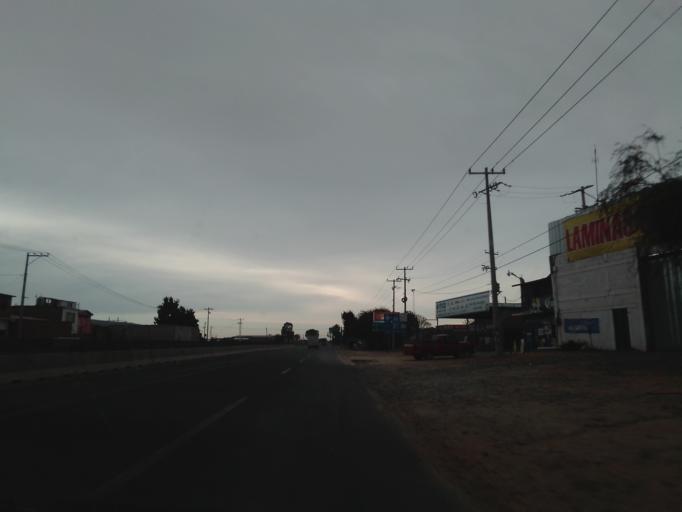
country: MX
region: Guanajuato
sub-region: Dolores Hidalgo Cuna de la Independencia Nacional
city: Ejido Jesus Maria
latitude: 21.1911
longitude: -100.8685
